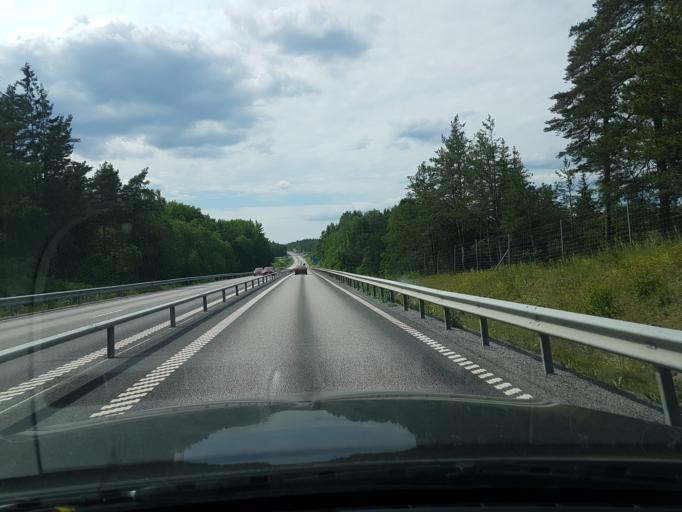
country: SE
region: Stockholm
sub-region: Norrtalje Kommun
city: Norrtalje
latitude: 59.7303
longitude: 18.8035
